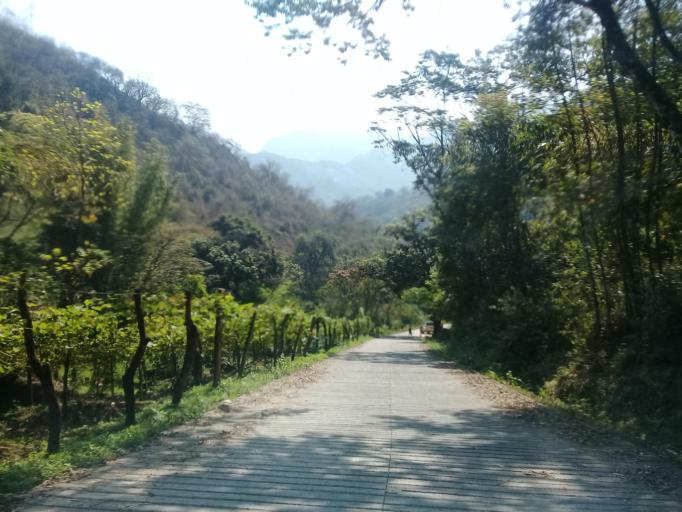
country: MX
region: Veracruz
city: Rafael Delgado
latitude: 18.7815
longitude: -97.0245
